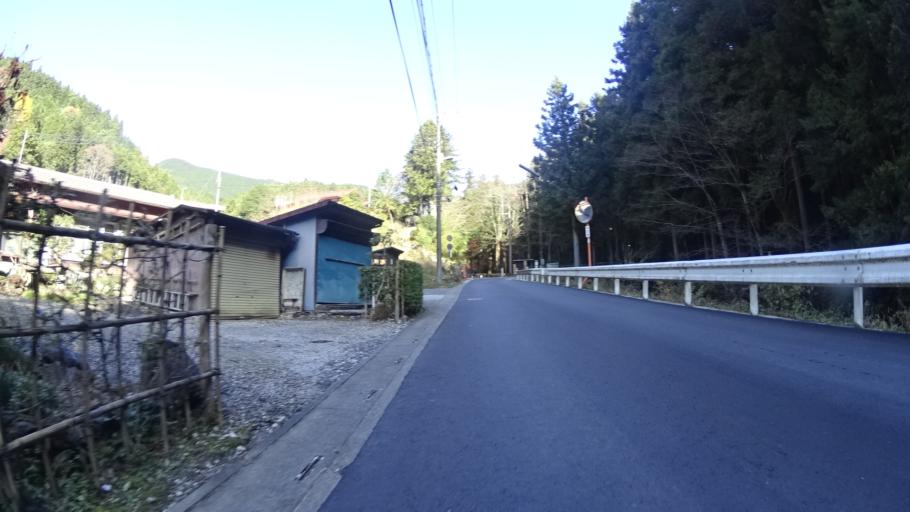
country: JP
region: Saitama
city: Chichibu
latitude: 35.9200
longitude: 139.1509
